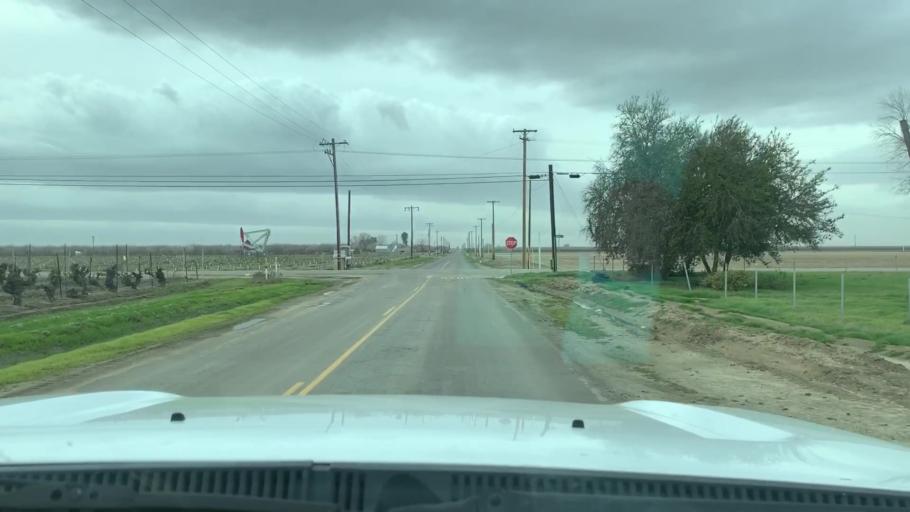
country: US
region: California
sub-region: Kern County
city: Shafter
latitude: 35.5292
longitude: -119.2773
